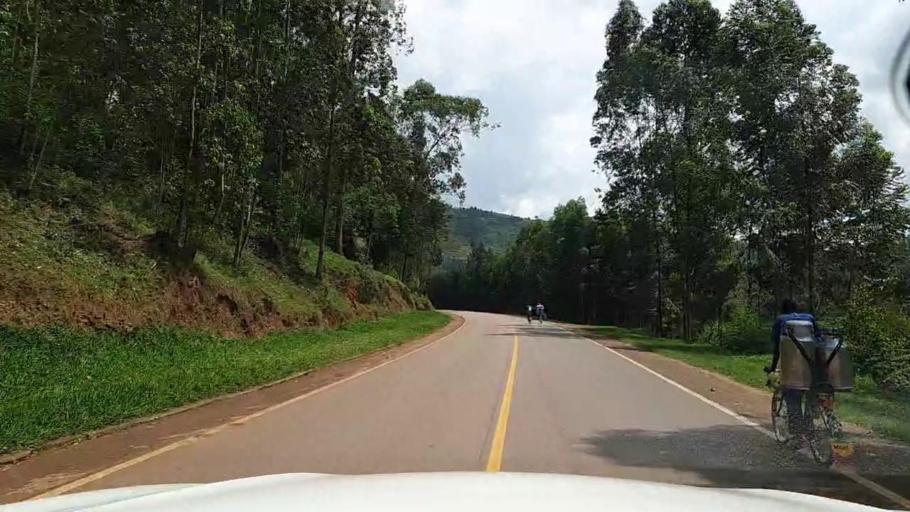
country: RW
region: Kigali
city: Kigali
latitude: -1.8156
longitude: 30.0942
